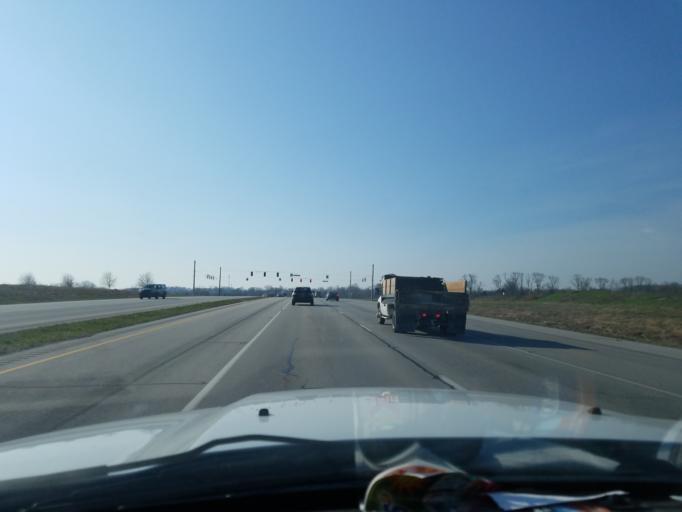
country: US
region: Indiana
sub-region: Monroe County
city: Bloomington
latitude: 39.1951
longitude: -86.5722
